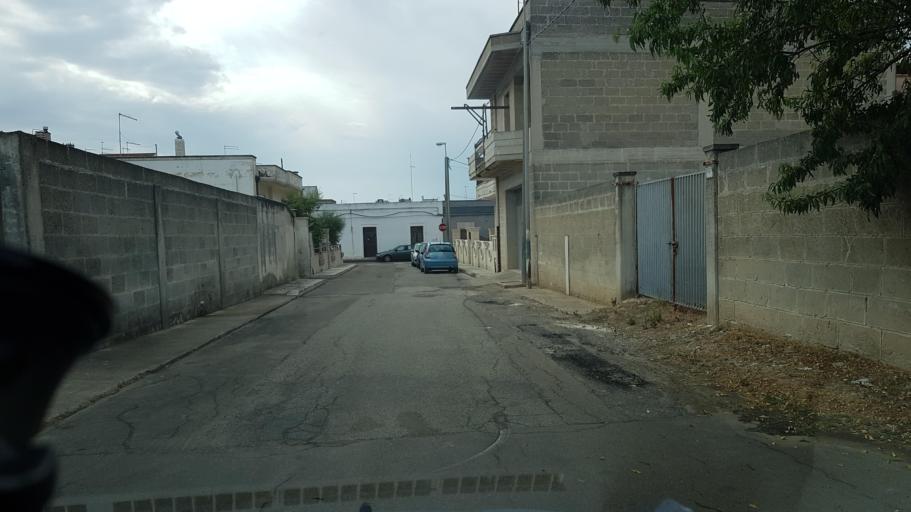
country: IT
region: Apulia
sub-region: Provincia di Brindisi
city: Torre Santa Susanna
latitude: 40.4721
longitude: 17.7415
